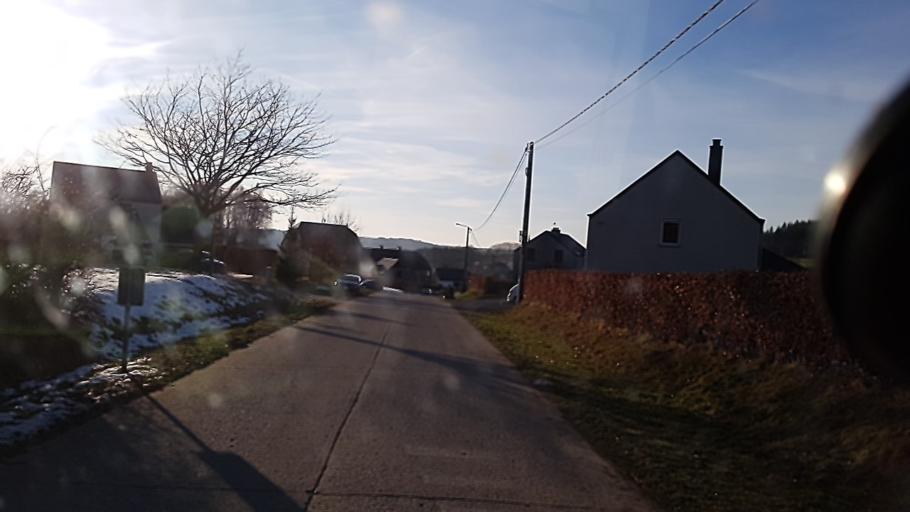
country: BE
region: Wallonia
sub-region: Province du Luxembourg
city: Daverdisse
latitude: 50.0061
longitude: 5.1682
